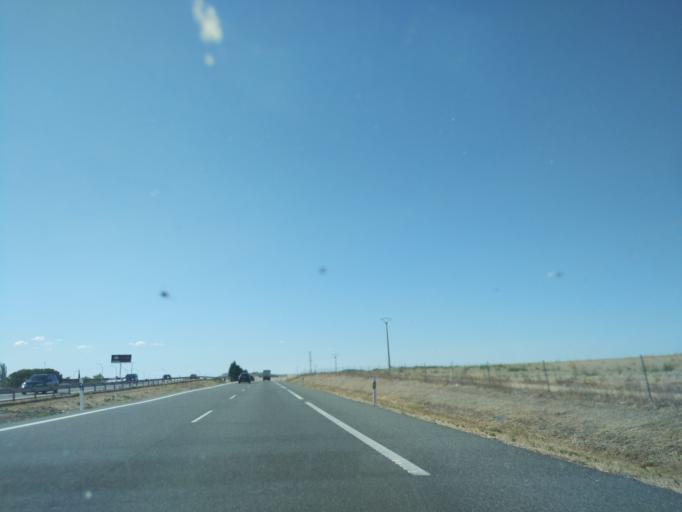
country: ES
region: Castille and Leon
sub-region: Provincia de Valladolid
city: Vega de Valdetronco
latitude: 41.5737
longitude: -5.0957
